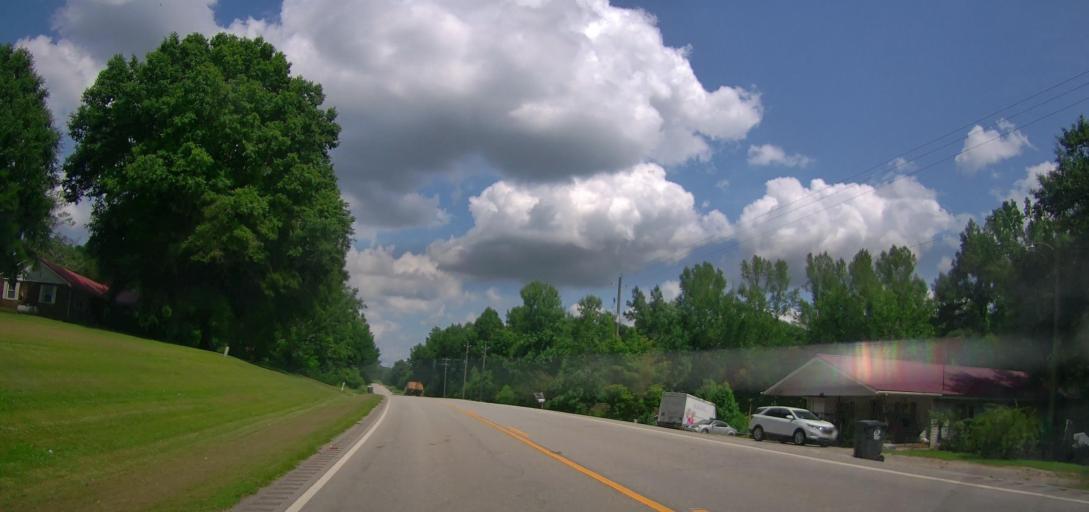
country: US
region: Alabama
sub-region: Cleburne County
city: Heflin
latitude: 33.5763
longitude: -85.4582
